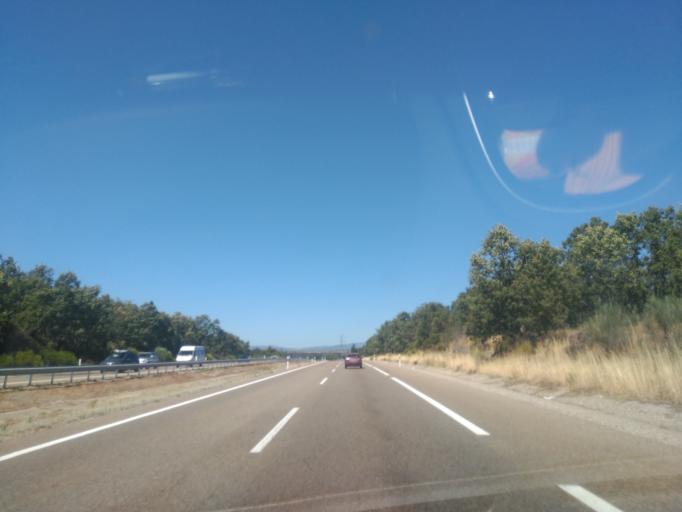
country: ES
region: Castille and Leon
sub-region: Provincia de Zamora
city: Mombuey
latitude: 42.0223
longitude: -6.3652
